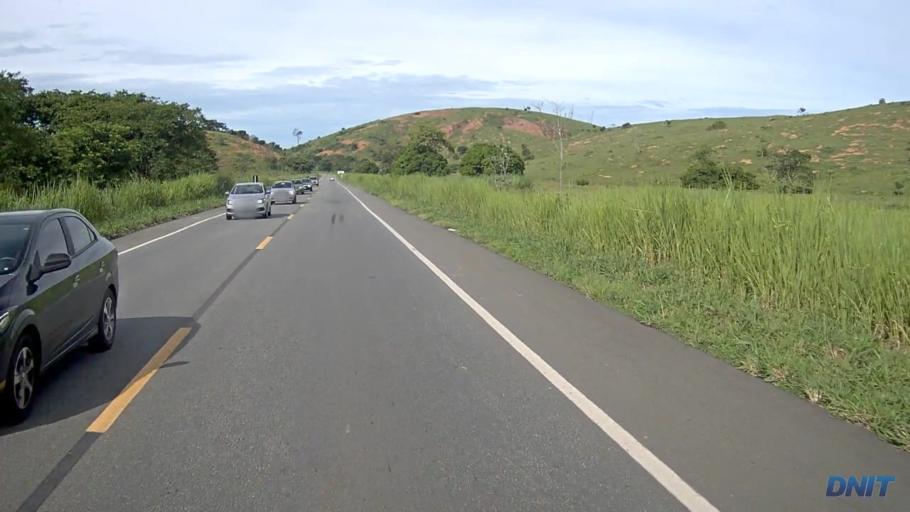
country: BR
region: Minas Gerais
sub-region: Belo Oriente
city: Belo Oriente
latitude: -19.2052
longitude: -42.2959
